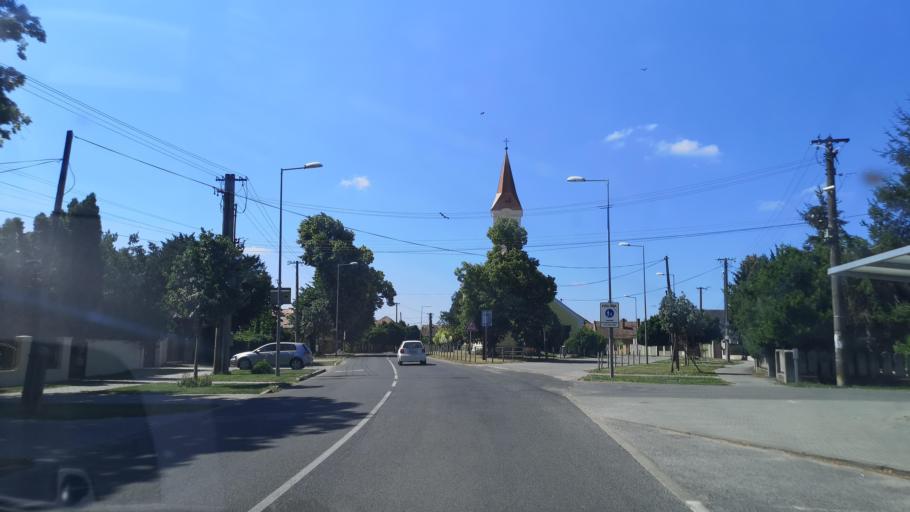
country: SK
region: Trnavsky
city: Samorin
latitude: 48.0541
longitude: 17.4602
